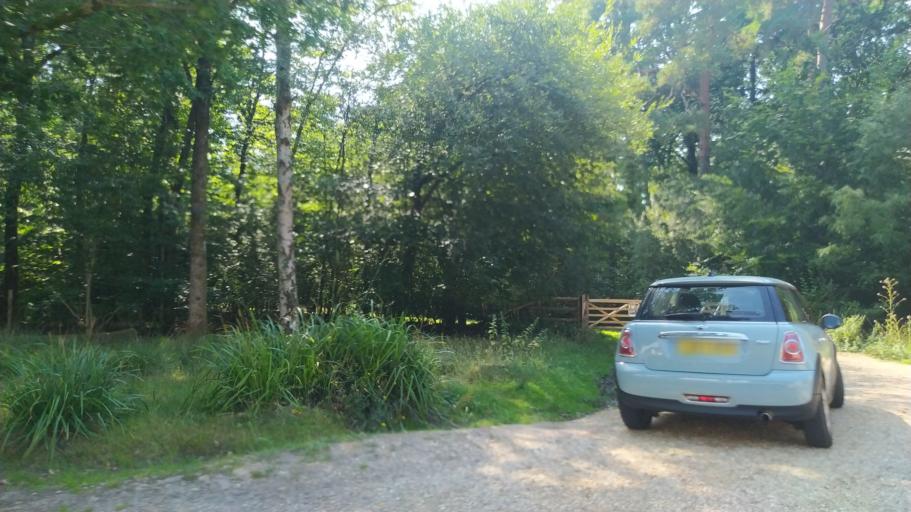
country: GB
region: England
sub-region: Hampshire
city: Totton
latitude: 50.8957
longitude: -1.5335
